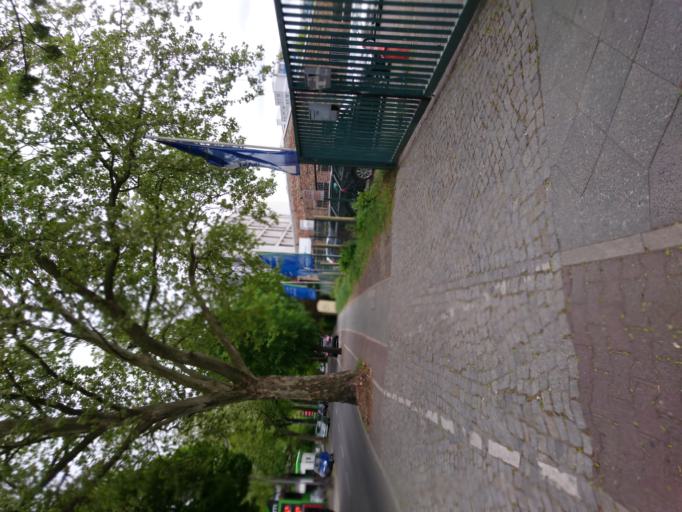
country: DE
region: Berlin
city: Tegel
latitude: 52.5775
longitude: 13.3057
